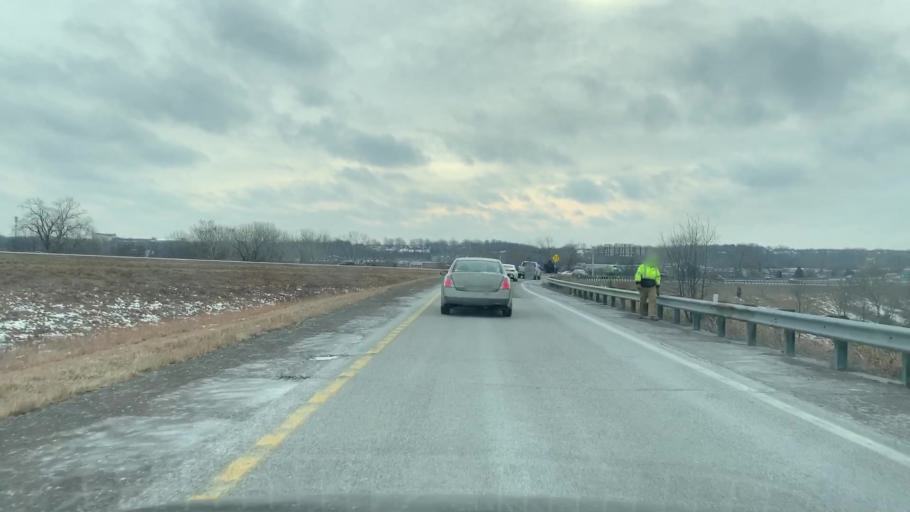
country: US
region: Missouri
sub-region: Jackson County
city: East Independence
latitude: 39.0392
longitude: -94.3633
